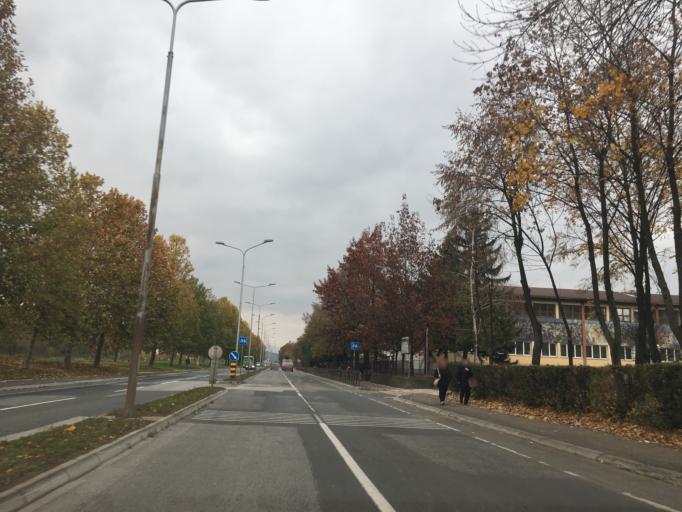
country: RS
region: Central Serbia
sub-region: Raski Okrug
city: Kraljevo
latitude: 43.7255
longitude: 20.7048
